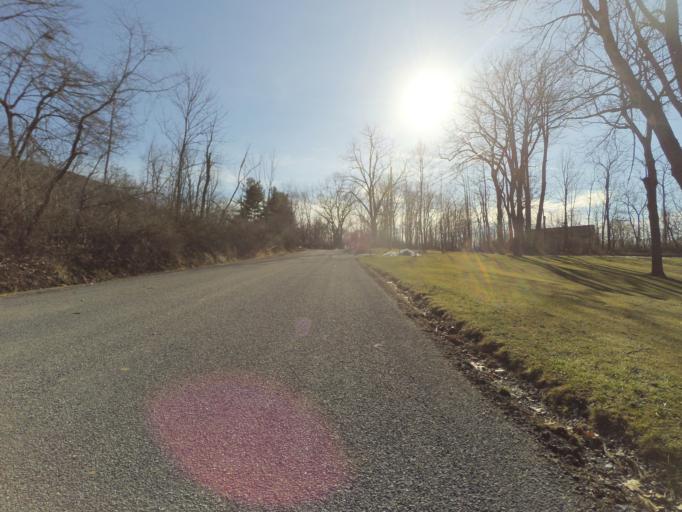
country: US
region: Pennsylvania
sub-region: Centre County
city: Lemont
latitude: 40.8154
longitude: -77.8057
